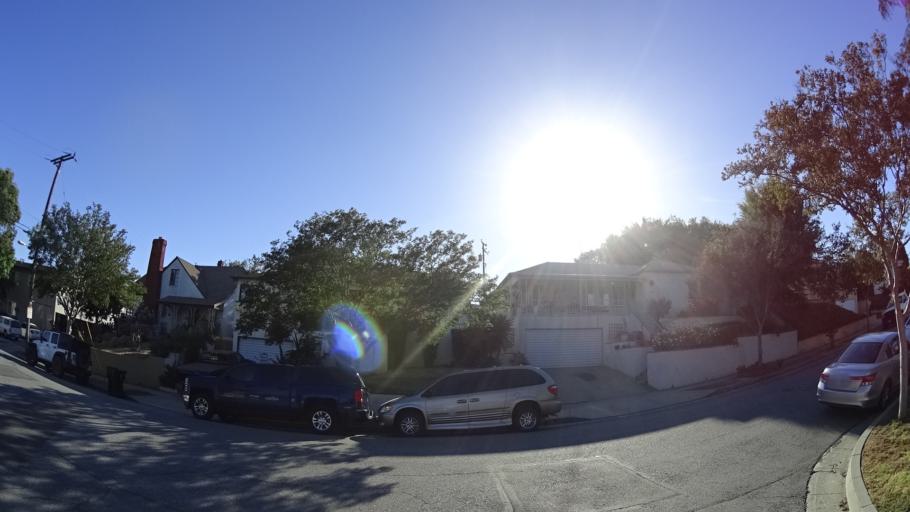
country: US
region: California
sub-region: Los Angeles County
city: Belvedere
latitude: 34.0655
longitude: -118.1585
